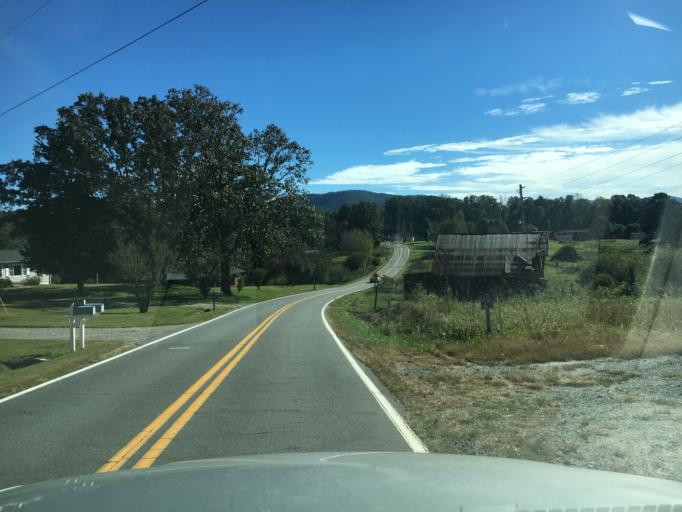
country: US
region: North Carolina
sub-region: Burke County
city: Salem
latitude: 35.6893
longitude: -81.7333
